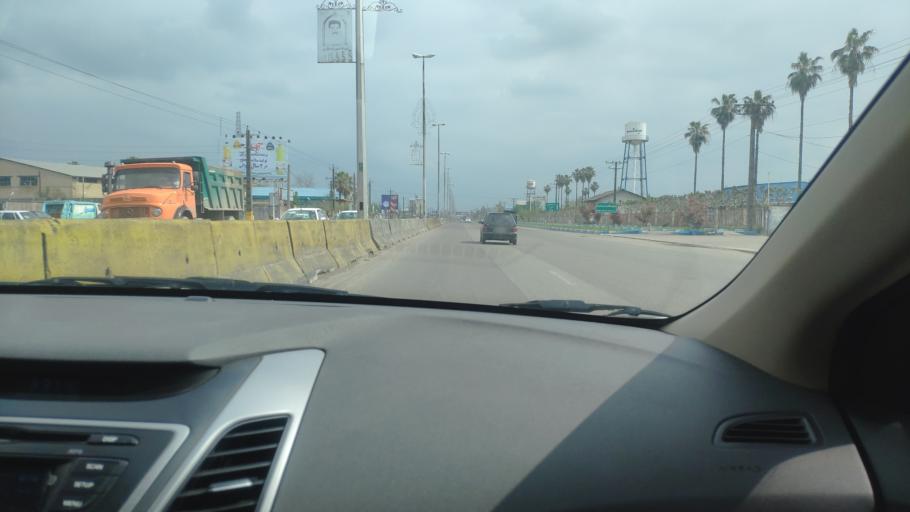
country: IR
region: Gilan
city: Rasht
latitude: 37.2341
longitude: 49.6277
